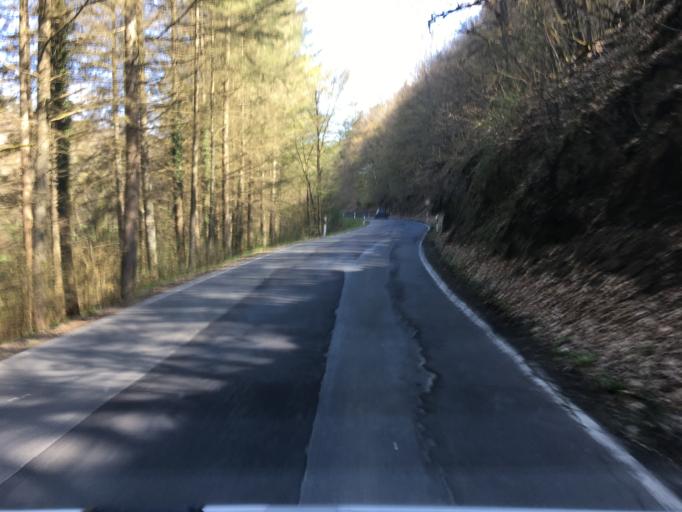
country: DE
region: Rheinland-Pfalz
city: Altenahr
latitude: 50.5101
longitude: 6.9680
